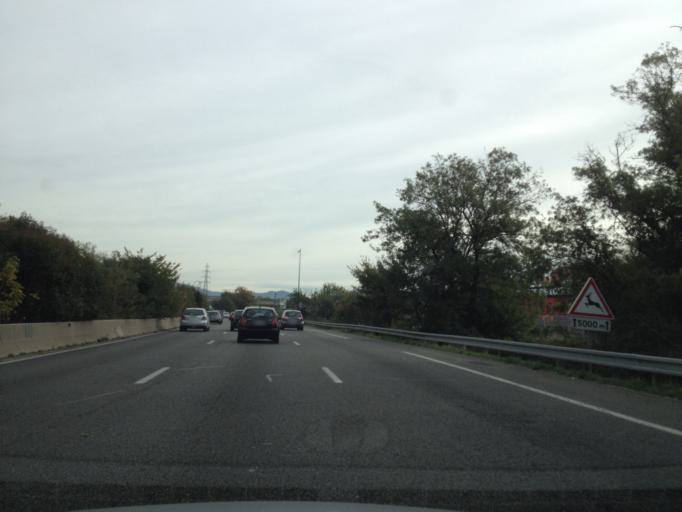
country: FR
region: Provence-Alpes-Cote d'Azur
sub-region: Departement des Bouches-du-Rhone
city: La Penne-sur-Huveaune
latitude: 43.2846
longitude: 5.5202
